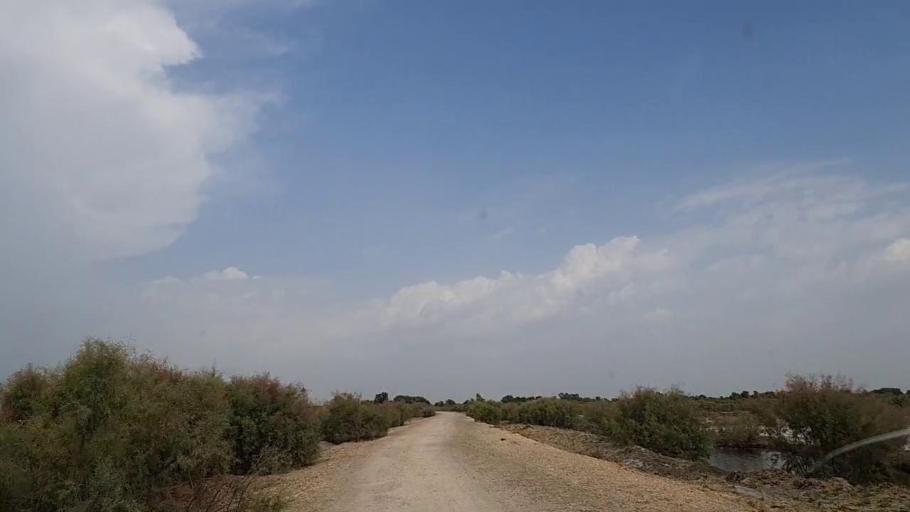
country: PK
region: Sindh
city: Khanpur
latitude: 27.8194
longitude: 69.5294
